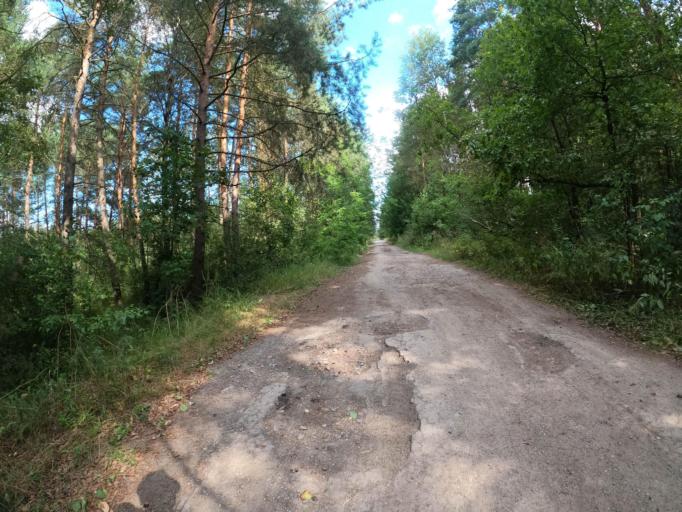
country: RU
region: Moskovskaya
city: Lopatinskiy
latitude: 55.3838
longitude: 38.7040
